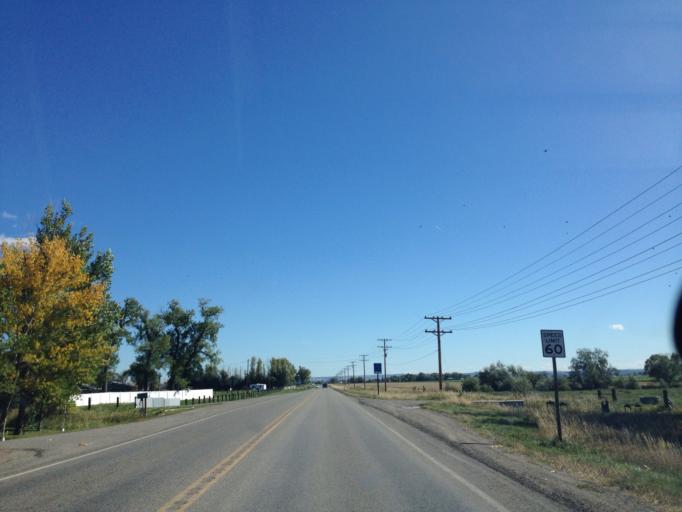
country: US
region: Montana
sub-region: Yellowstone County
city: Laurel
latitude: 45.7551
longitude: -108.6989
